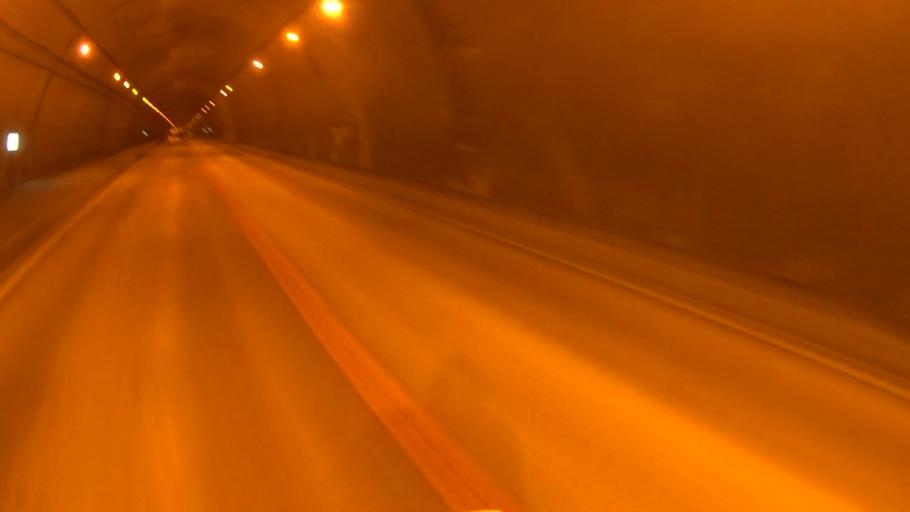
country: JP
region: Kyoto
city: Ayabe
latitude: 35.2664
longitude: 135.4024
